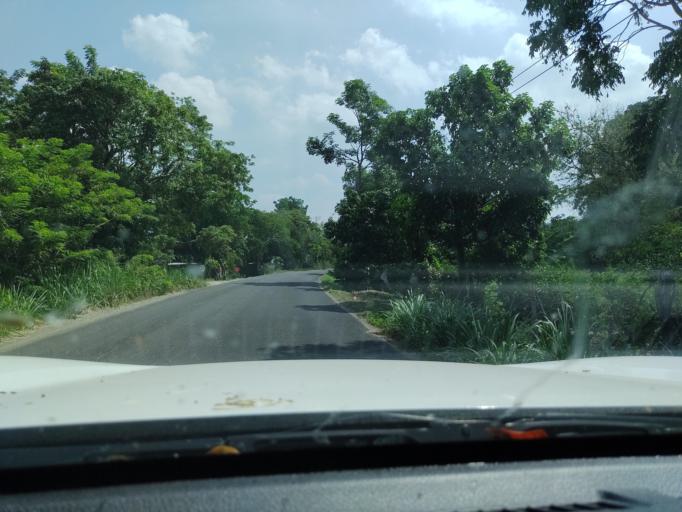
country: MX
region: Veracruz
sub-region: Atzalan
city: Colonias Pedernales
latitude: 20.0587
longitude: -97.0273
